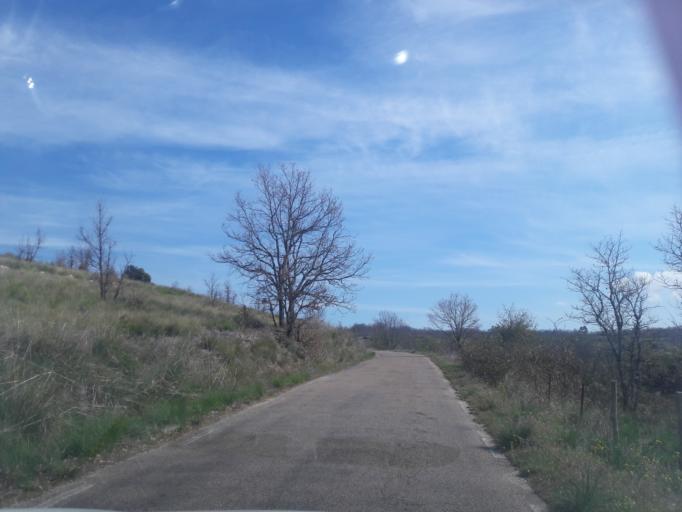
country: ES
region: Castille and Leon
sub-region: Provincia de Salamanca
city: San Esteban de la Sierra
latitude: 40.5082
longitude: -5.8695
